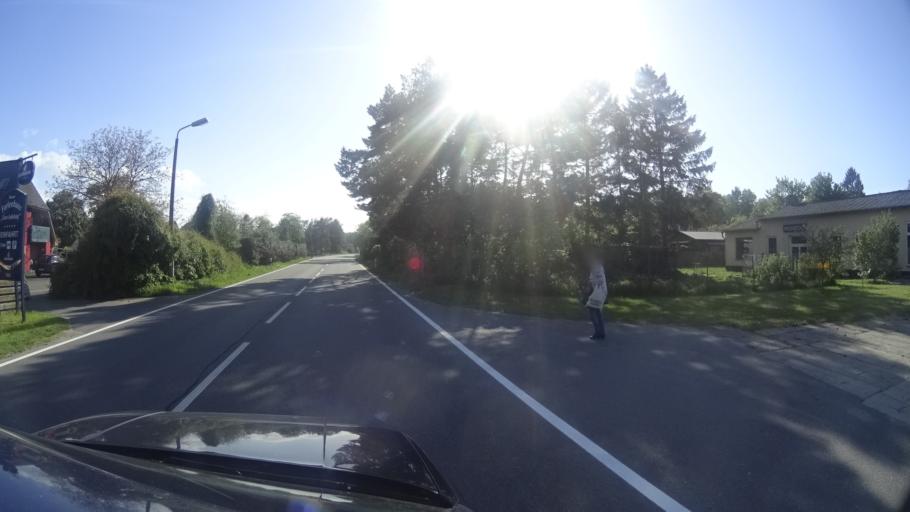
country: DE
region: Mecklenburg-Vorpommern
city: Born
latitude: 54.3915
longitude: 12.5392
